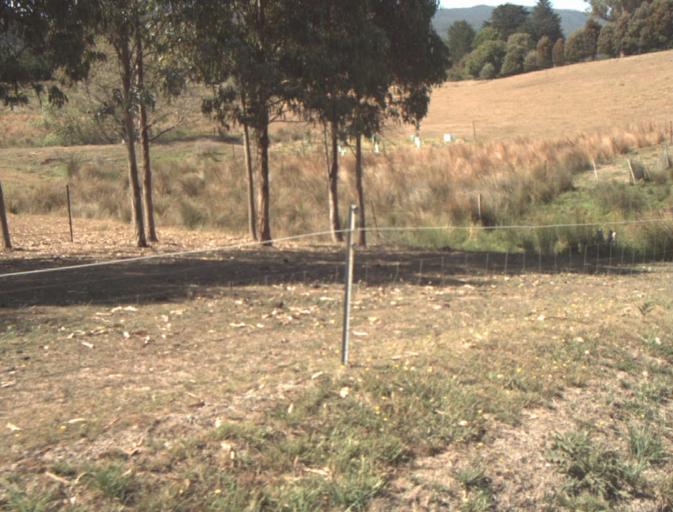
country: AU
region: Tasmania
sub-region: Launceston
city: Mayfield
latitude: -41.2276
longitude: 147.2362
